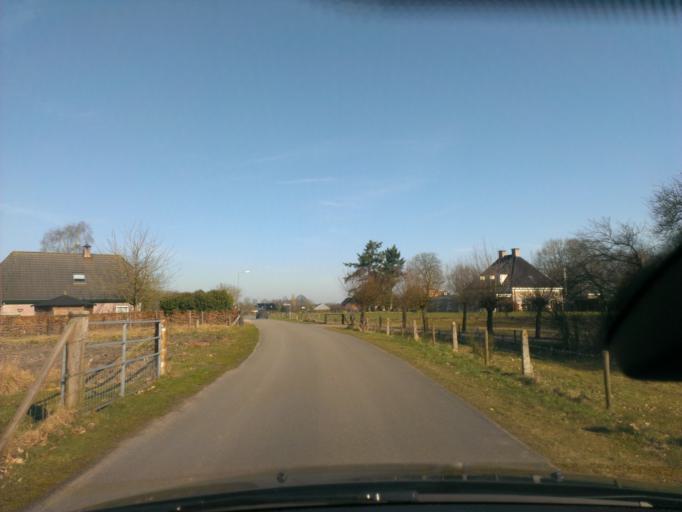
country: NL
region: Gelderland
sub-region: Gemeente Heerde
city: Heerde
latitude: 52.4186
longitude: 6.0695
